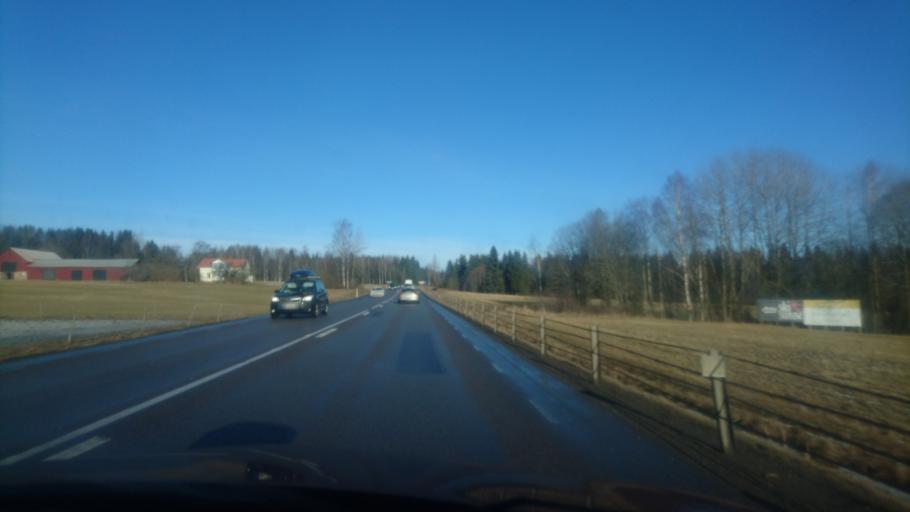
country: SE
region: Vaermland
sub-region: Sunne Kommun
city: Sunne
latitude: 59.7841
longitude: 13.0982
